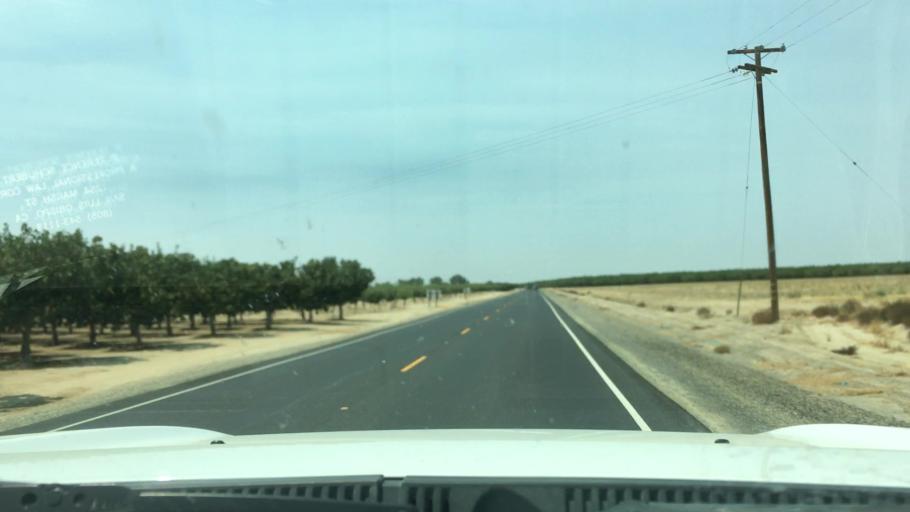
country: US
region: California
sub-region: Kern County
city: Lost Hills
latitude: 35.6084
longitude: -119.5814
